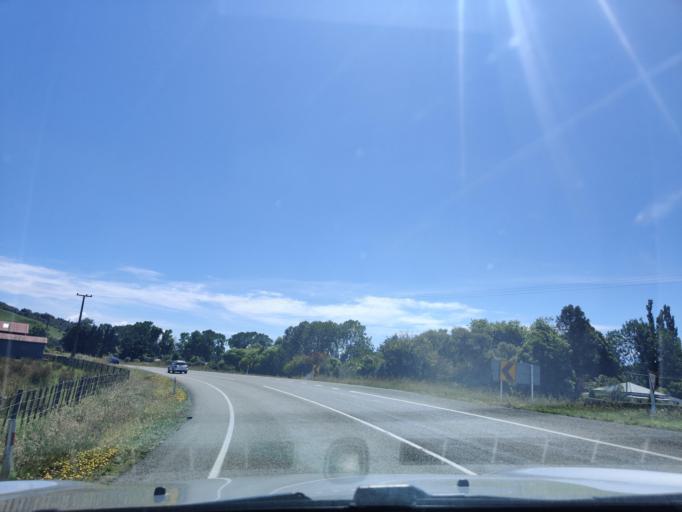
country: NZ
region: Manawatu-Wanganui
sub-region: Rangitikei District
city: Bulls
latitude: -39.9321
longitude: 175.5756
